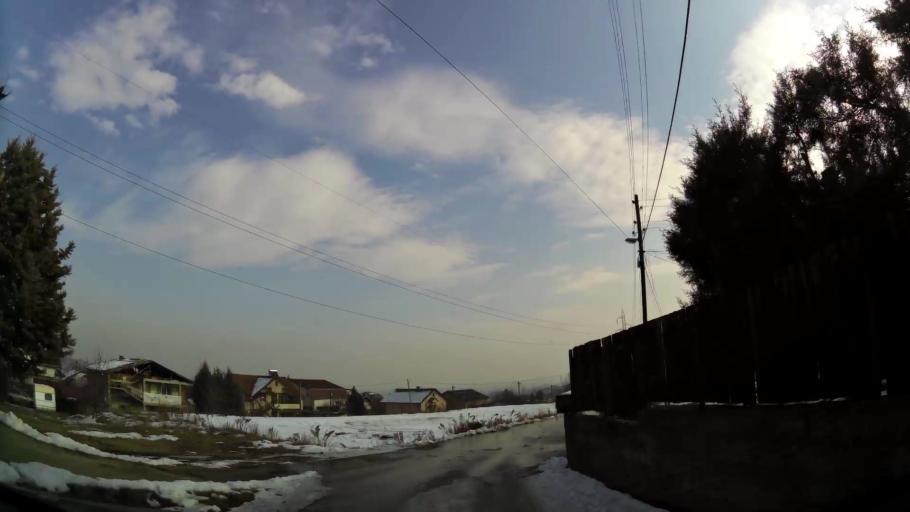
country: MK
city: Creshevo
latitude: 42.0088
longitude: 21.4981
